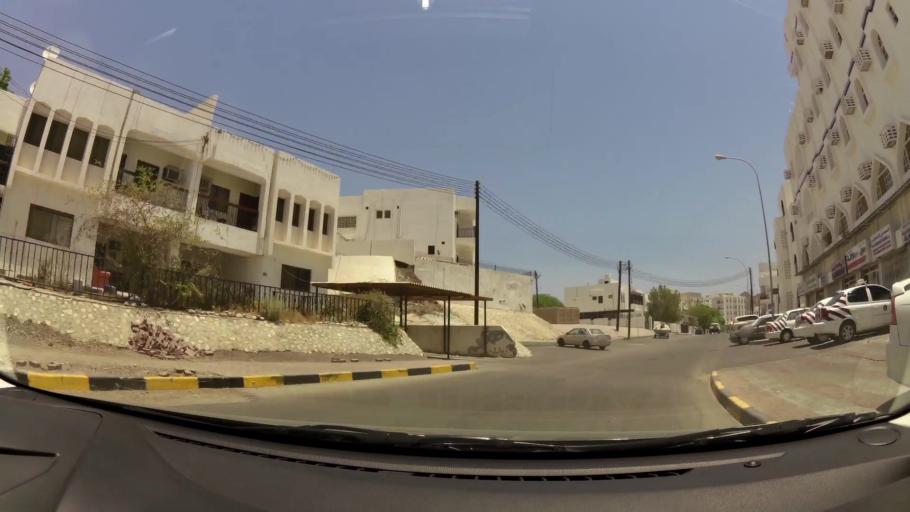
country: OM
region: Muhafazat Masqat
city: Muscat
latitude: 23.6113
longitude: 58.5431
